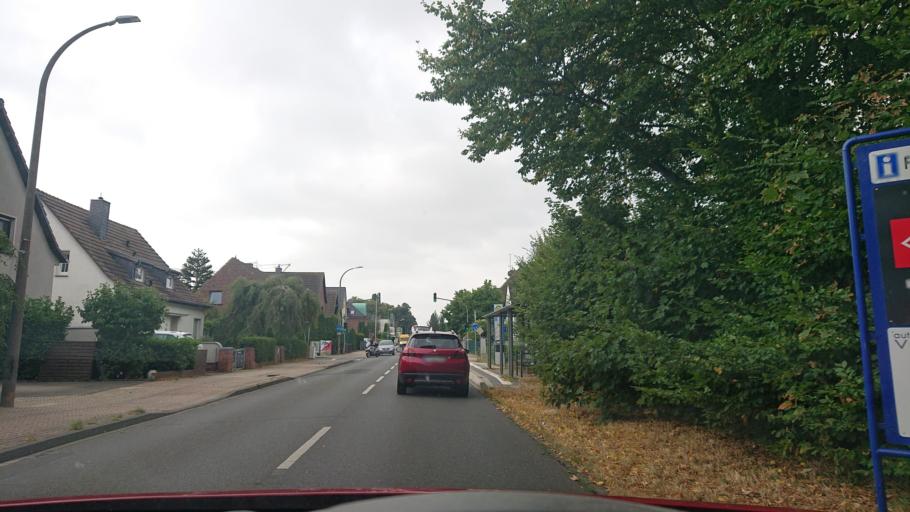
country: DE
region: North Rhine-Westphalia
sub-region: Regierungsbezirk Koln
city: Erftstadt
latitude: 50.8061
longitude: 6.7653
